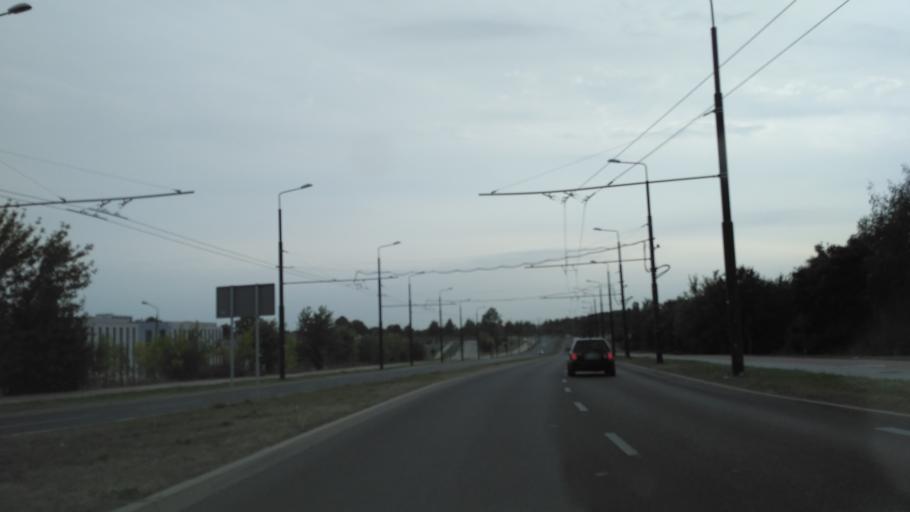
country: PL
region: Lublin Voivodeship
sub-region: Powiat lubelski
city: Jakubowice Murowane
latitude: 51.2274
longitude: 22.6183
